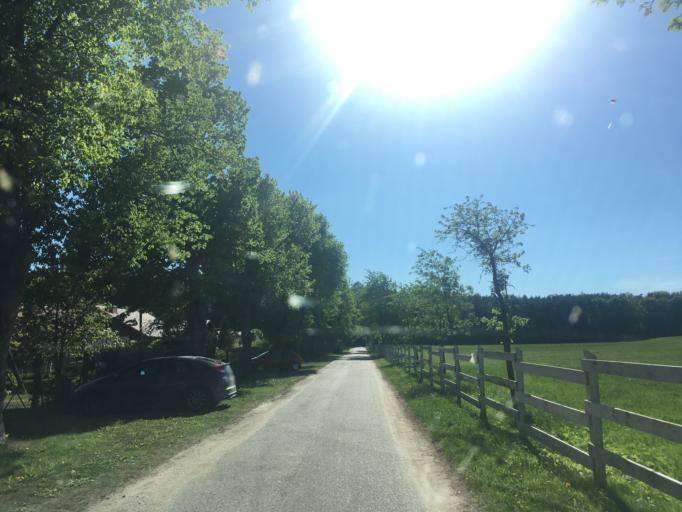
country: PL
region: Warmian-Masurian Voivodeship
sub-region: Powiat mragowski
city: Mikolajki
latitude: 53.7500
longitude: 21.6242
